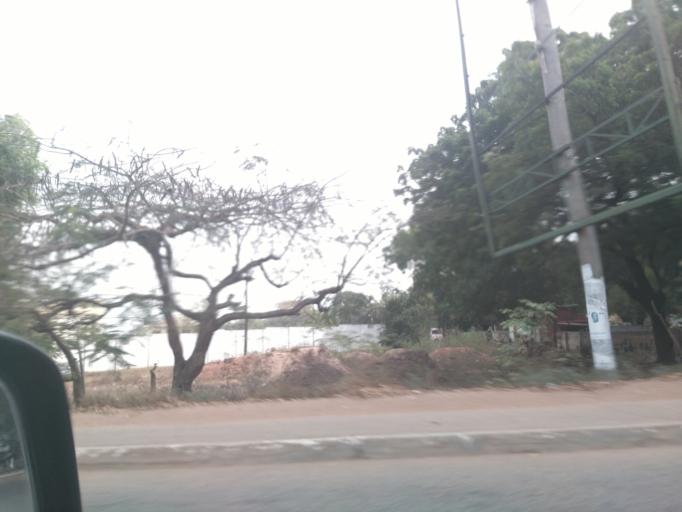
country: GH
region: Greater Accra
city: Accra
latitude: 5.5924
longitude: -0.1838
